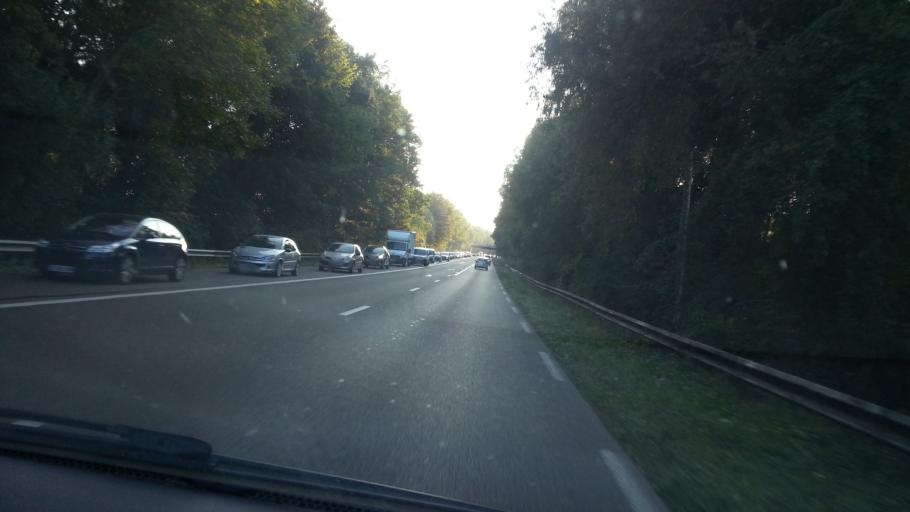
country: FR
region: Picardie
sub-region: Departement de l'Oise
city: Brenouille
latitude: 49.3116
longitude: 2.5500
